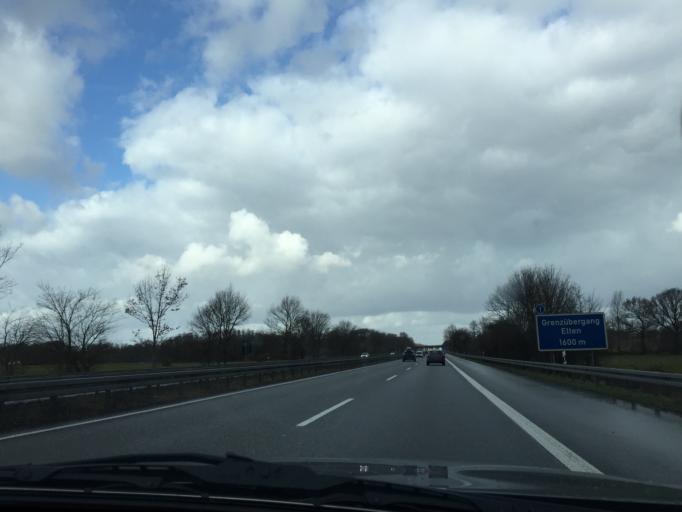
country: NL
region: Gelderland
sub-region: Gemeente Montferland
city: s-Heerenberg
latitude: 51.8887
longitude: 6.1761
